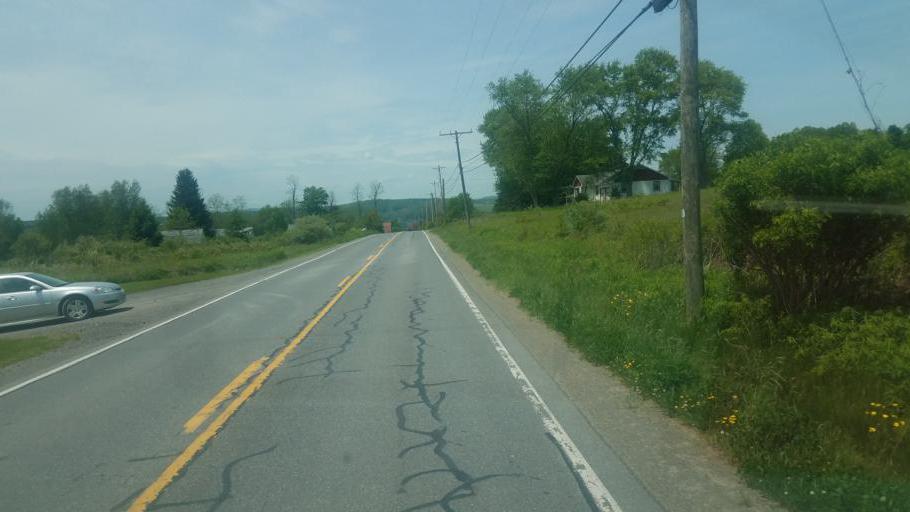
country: US
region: Pennsylvania
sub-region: Tioga County
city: Wellsboro
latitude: 41.7700
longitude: -77.2187
